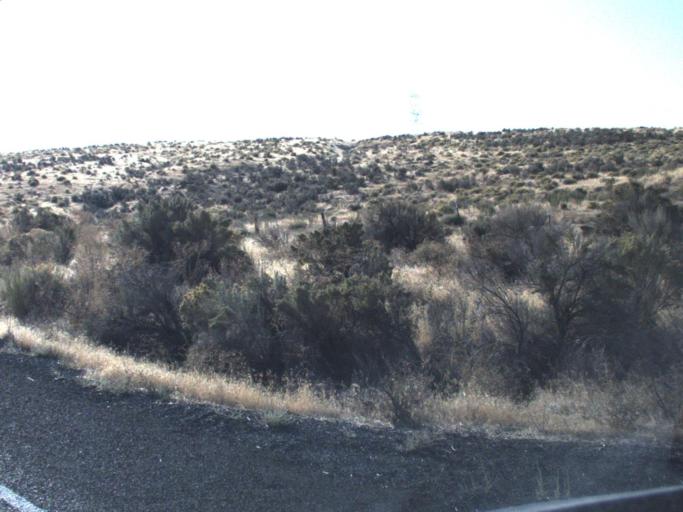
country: US
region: Washington
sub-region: Franklin County
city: Connell
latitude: 46.6442
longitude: -118.8316
